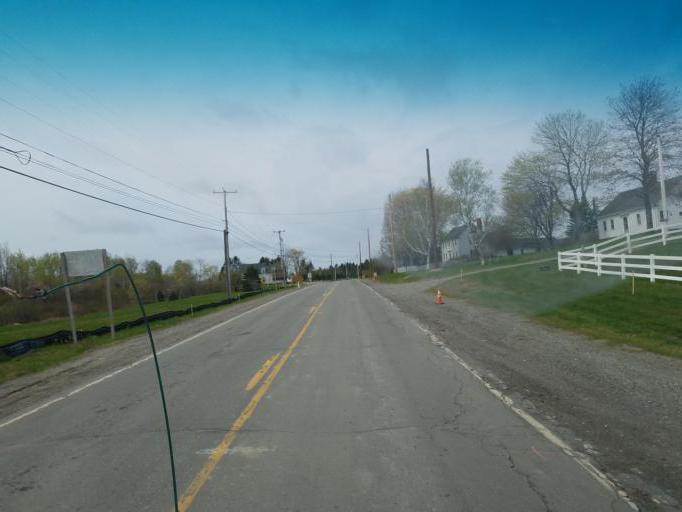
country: US
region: Maine
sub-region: Washington County
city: East Machias
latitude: 44.7901
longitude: -67.1781
